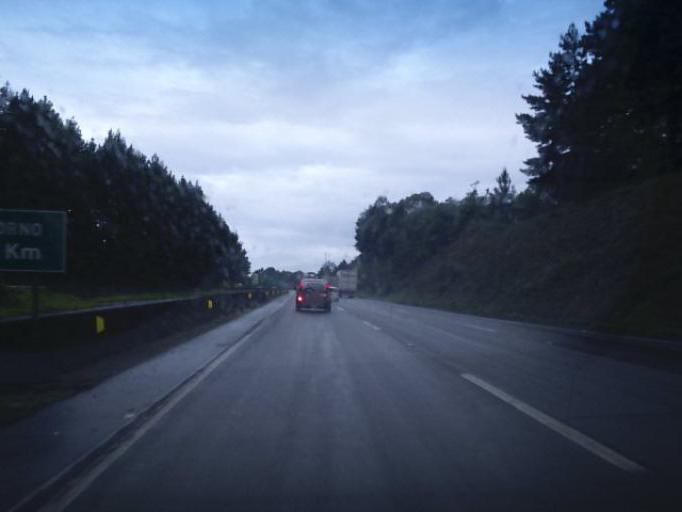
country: BR
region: Parana
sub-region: Sao Jose Dos Pinhais
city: Sao Jose dos Pinhais
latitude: -25.8435
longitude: -49.0523
